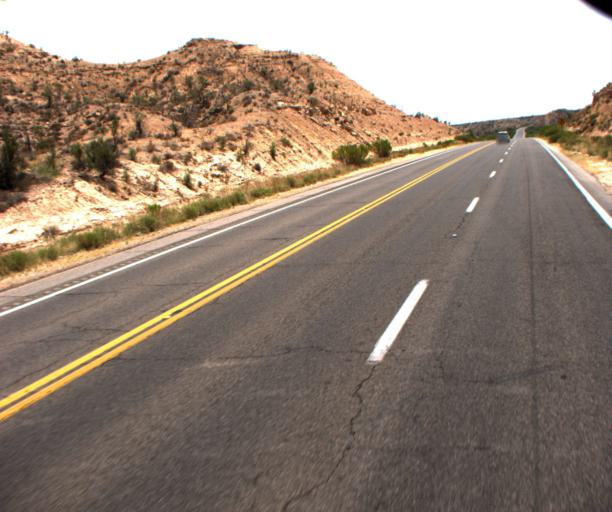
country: US
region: Arizona
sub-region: Gila County
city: San Carlos
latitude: 33.3457
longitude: -110.6197
